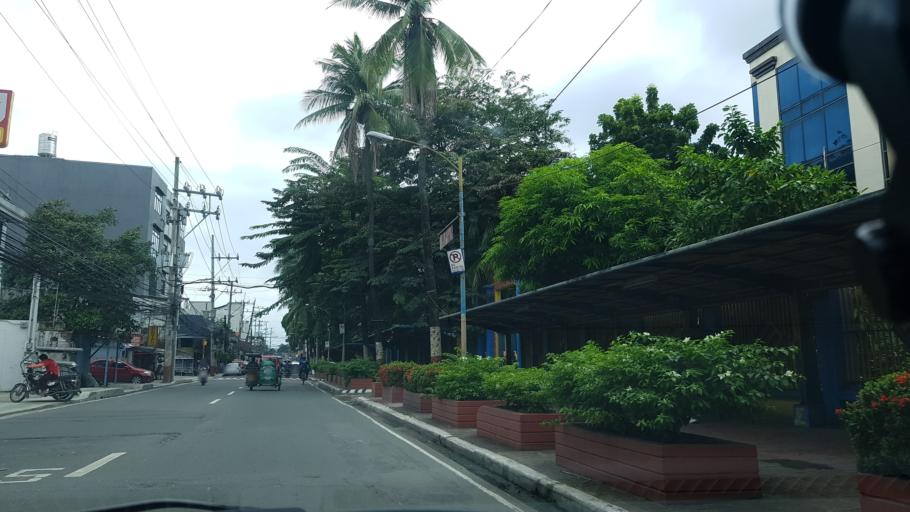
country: PH
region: Metro Manila
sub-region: Pasig
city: Pasig City
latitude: 14.5682
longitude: 121.0764
